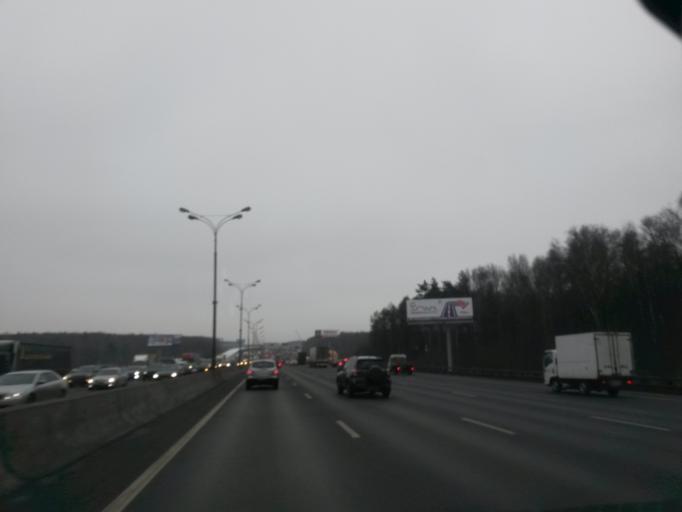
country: RU
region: Moskovskaya
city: Vostryakovo
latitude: 55.6472
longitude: 37.4499
